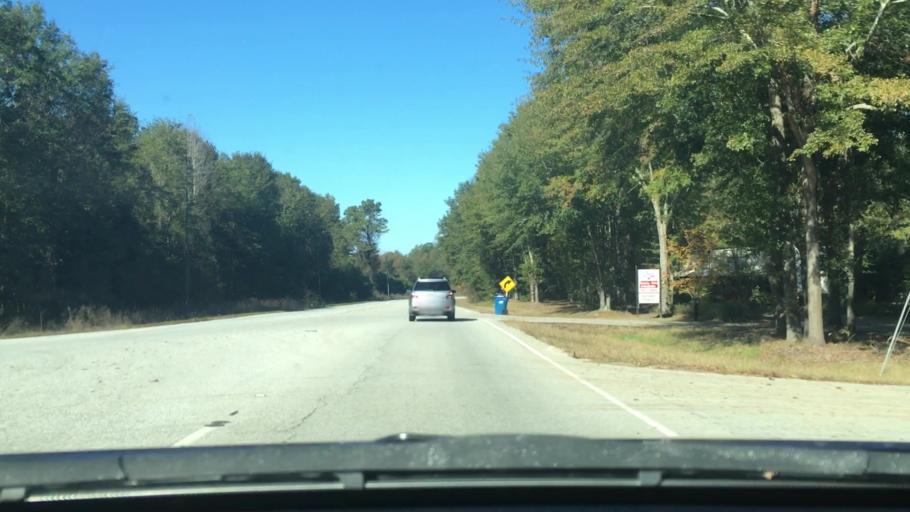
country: US
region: South Carolina
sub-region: Sumter County
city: Lakewood
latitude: 33.8723
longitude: -80.3648
